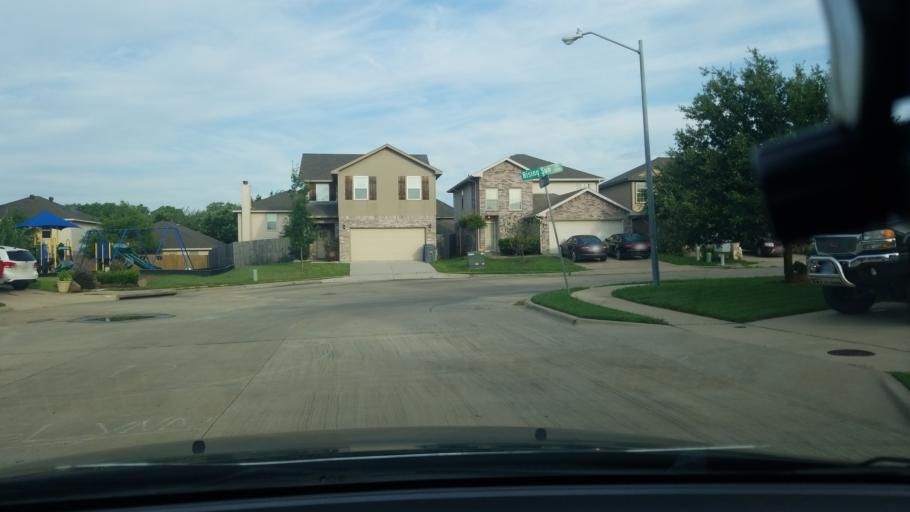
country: US
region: Texas
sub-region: Dallas County
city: Balch Springs
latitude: 32.7667
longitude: -96.6509
